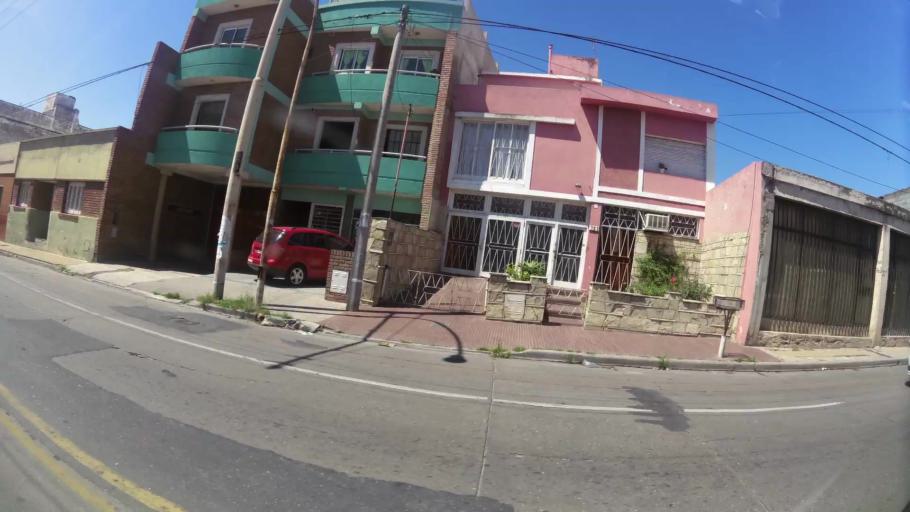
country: AR
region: Cordoba
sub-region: Departamento de Capital
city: Cordoba
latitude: -31.4287
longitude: -64.2025
